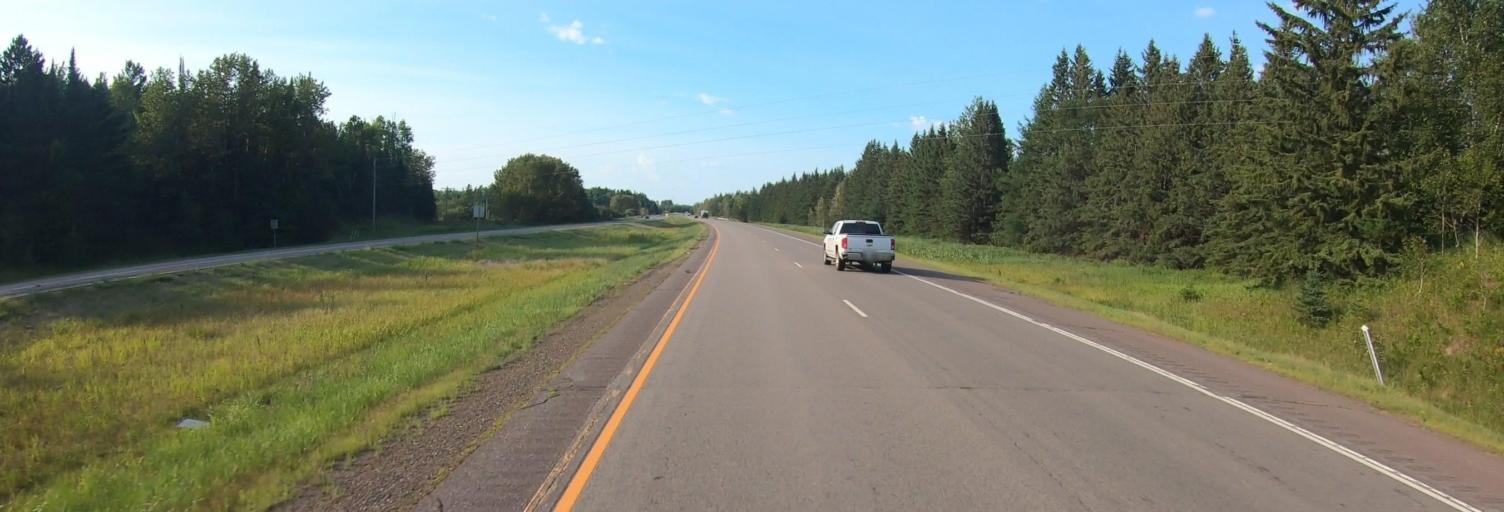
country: US
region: Minnesota
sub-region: Saint Louis County
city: Eveleth
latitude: 47.1294
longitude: -92.4723
